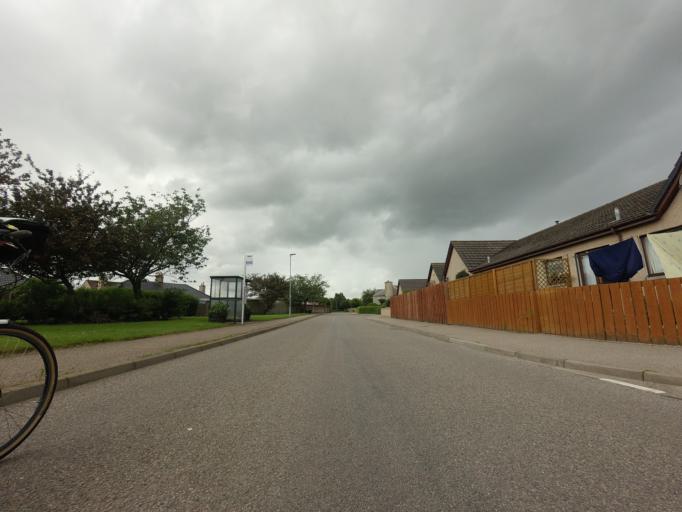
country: GB
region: Scotland
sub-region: Moray
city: Fochabers
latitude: 57.6626
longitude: -3.1151
